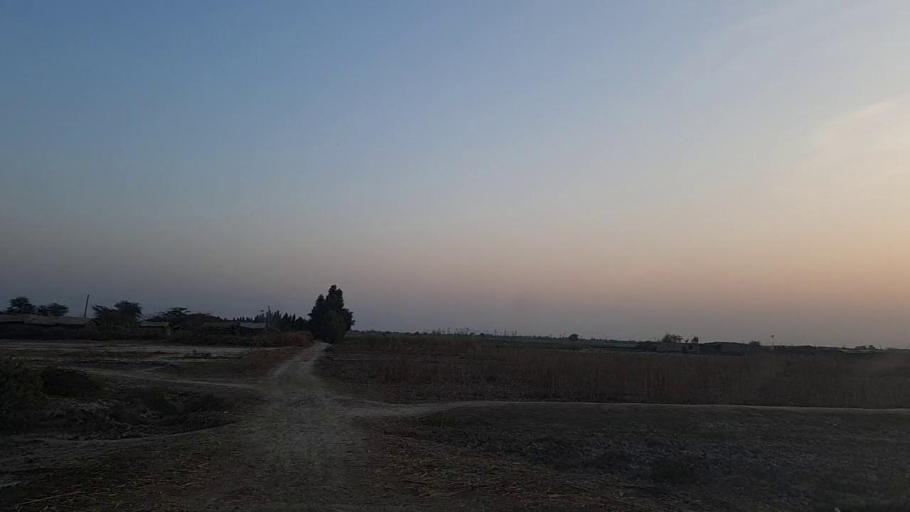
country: PK
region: Sindh
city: Naukot
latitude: 24.9700
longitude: 69.4273
